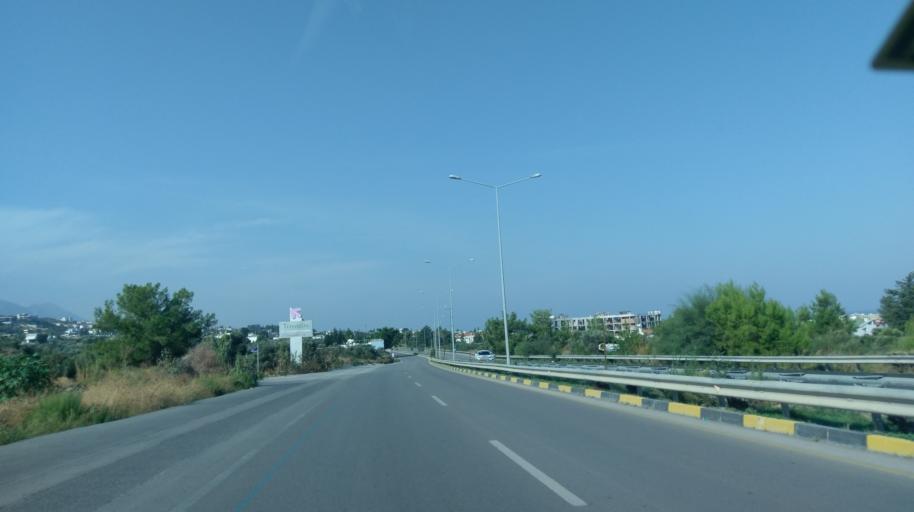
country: CY
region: Keryneia
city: Kyrenia
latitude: 35.3326
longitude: 33.2694
